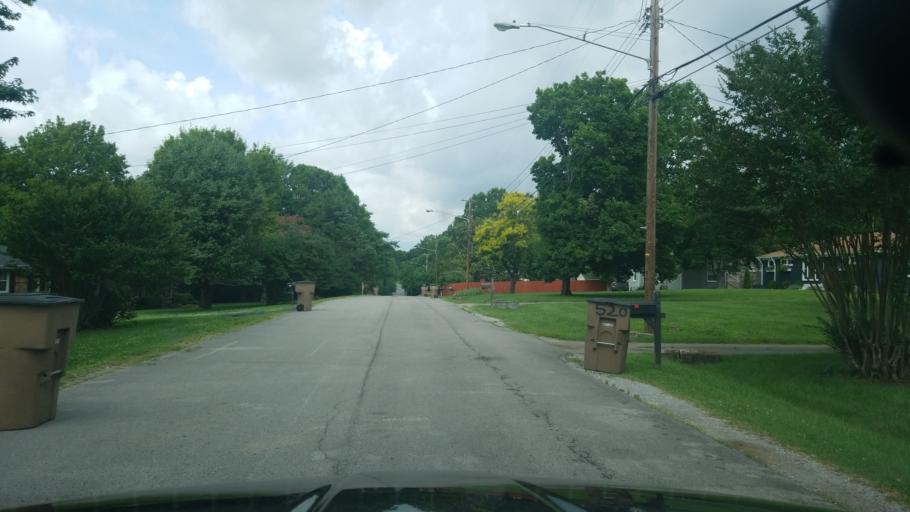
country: US
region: Tennessee
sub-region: Davidson County
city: Oak Hill
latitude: 36.0833
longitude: -86.7426
